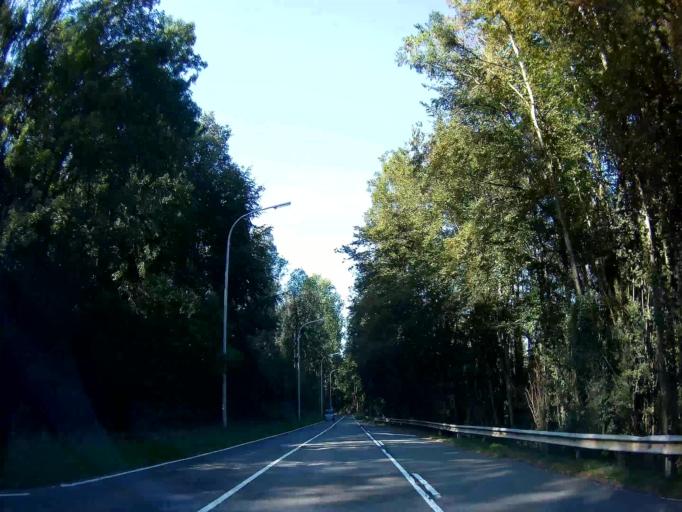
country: BE
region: Wallonia
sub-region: Province de Namur
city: Dinant
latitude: 50.2415
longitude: 4.9676
